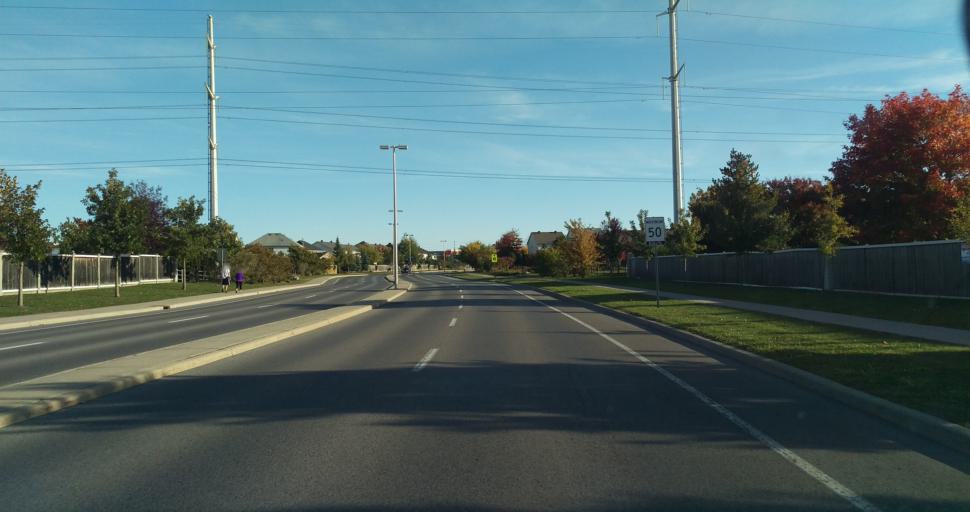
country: CA
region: Ontario
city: Clarence-Rockland
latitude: 45.4706
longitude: -75.4692
